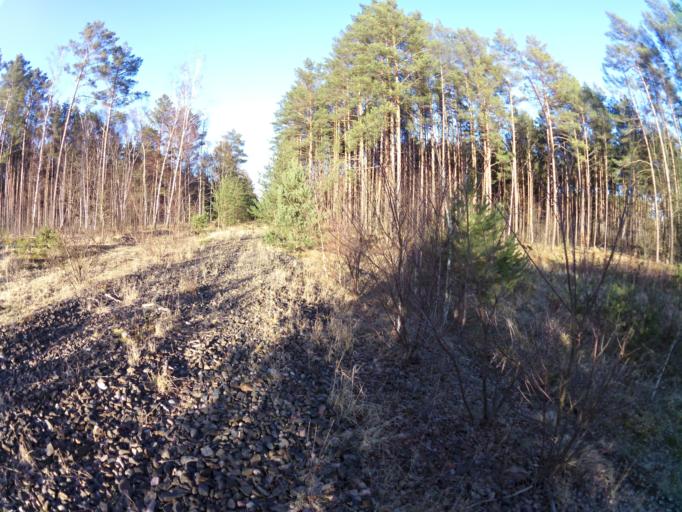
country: PL
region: West Pomeranian Voivodeship
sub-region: Powiat mysliborski
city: Debno
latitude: 52.8259
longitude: 14.7657
